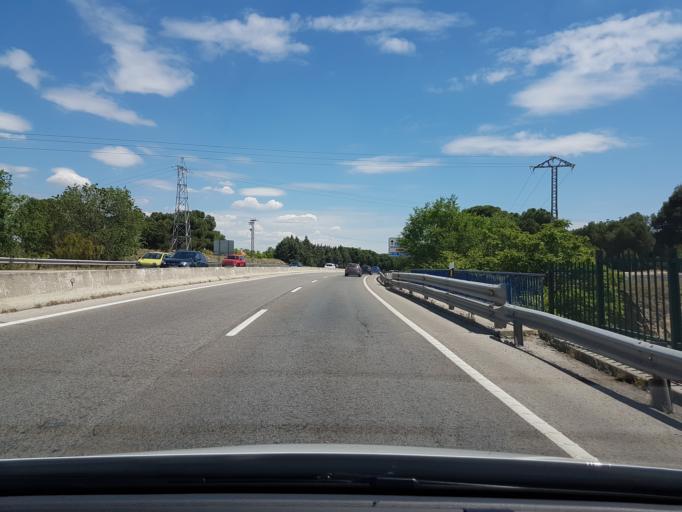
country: ES
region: Madrid
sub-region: Provincia de Madrid
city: Moncloa-Aravaca
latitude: 40.4474
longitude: -3.7673
